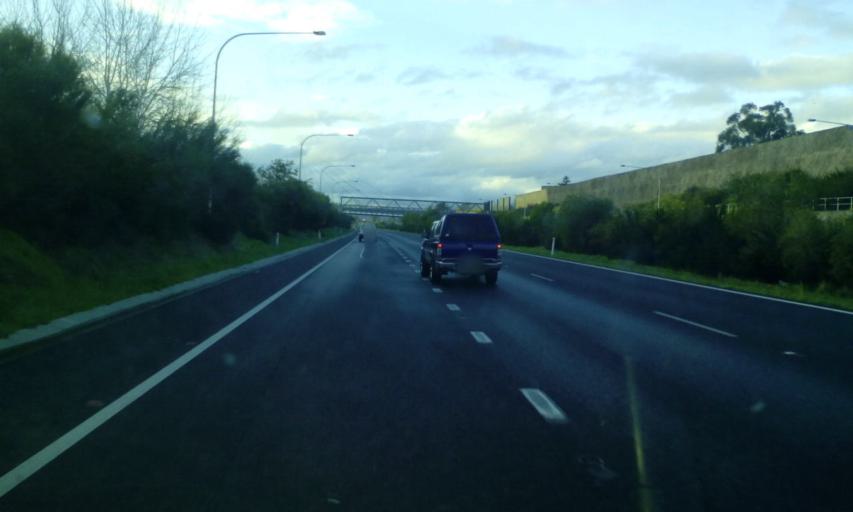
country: AU
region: New South Wales
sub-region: Albury Municipality
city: East Albury
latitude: -36.0857
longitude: 146.9252
